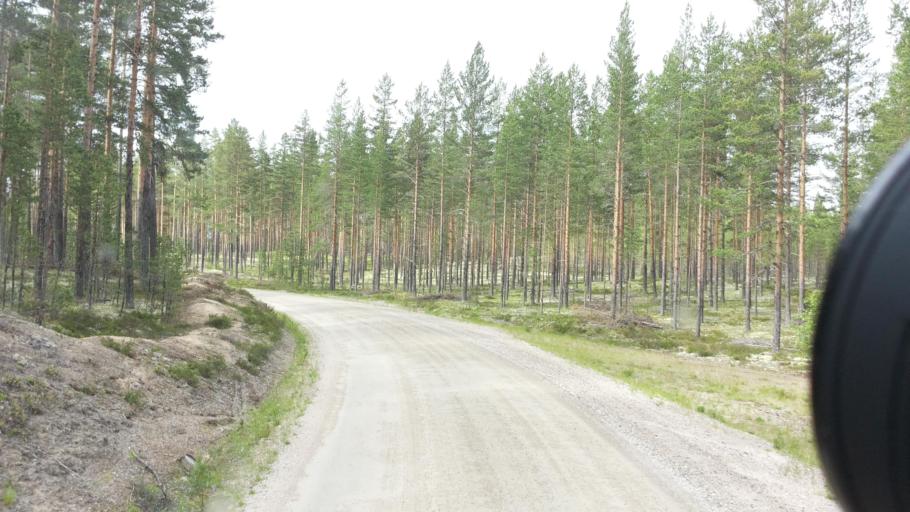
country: SE
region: Gaevleborg
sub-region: Ovanakers Kommun
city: Edsbyn
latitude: 61.5112
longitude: 15.3390
